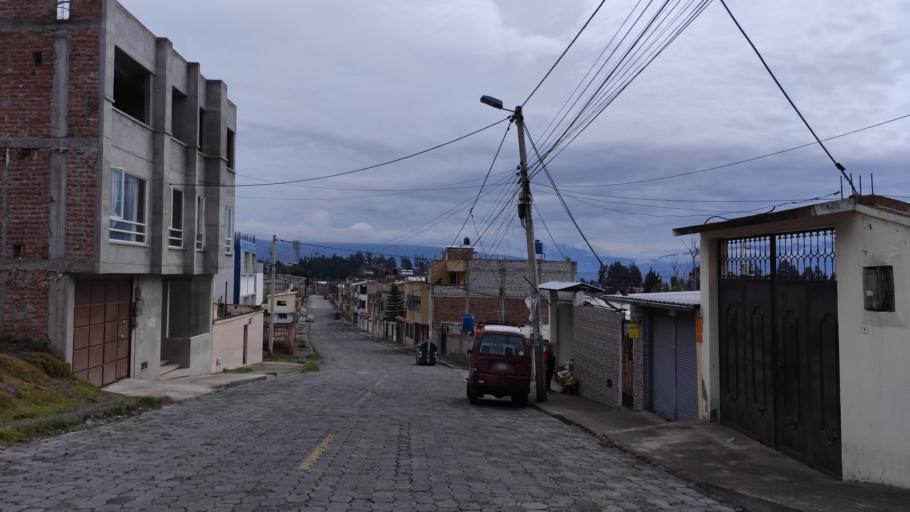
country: EC
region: Chimborazo
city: Riobamba
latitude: -1.6572
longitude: -78.6429
